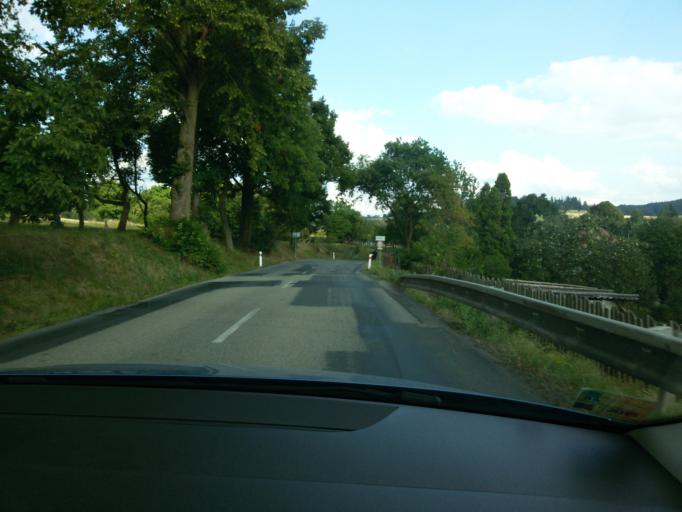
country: CZ
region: South Moravian
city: Olesnice
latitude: 49.5461
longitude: 16.4344
